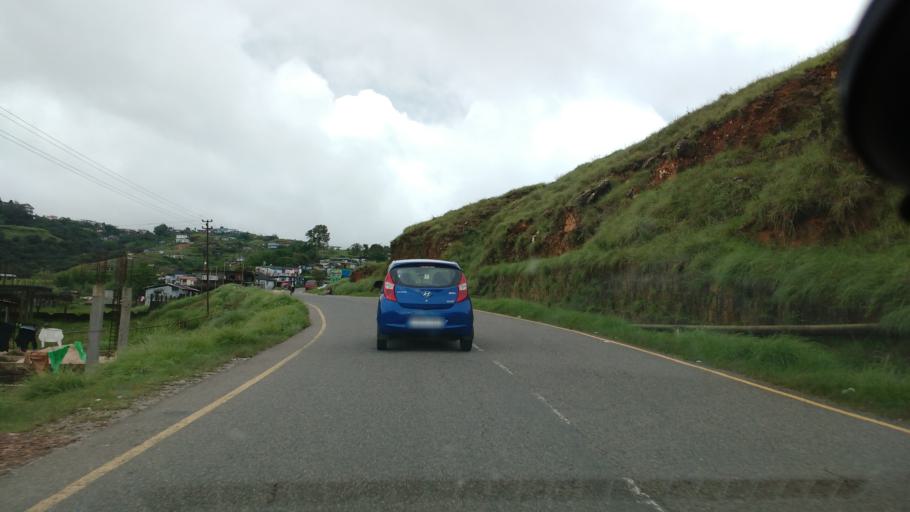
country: IN
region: Meghalaya
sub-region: East Khasi Hills
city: Cherrapunji
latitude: 25.2770
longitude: 91.7295
